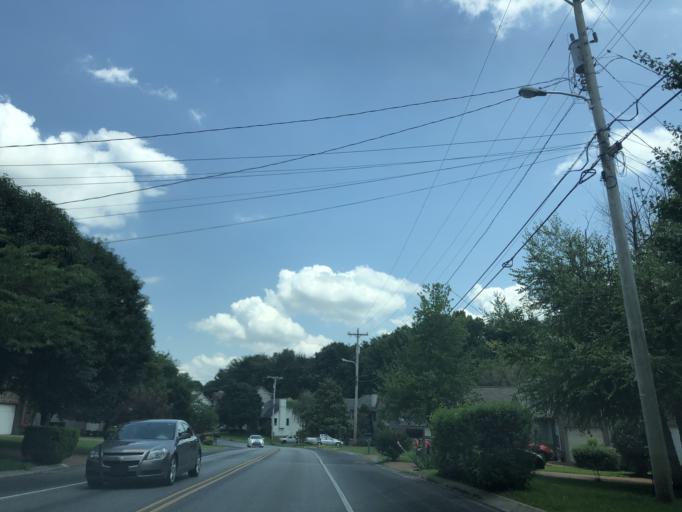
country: US
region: Tennessee
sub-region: Williamson County
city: Brentwood Estates
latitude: 36.0243
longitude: -86.7231
